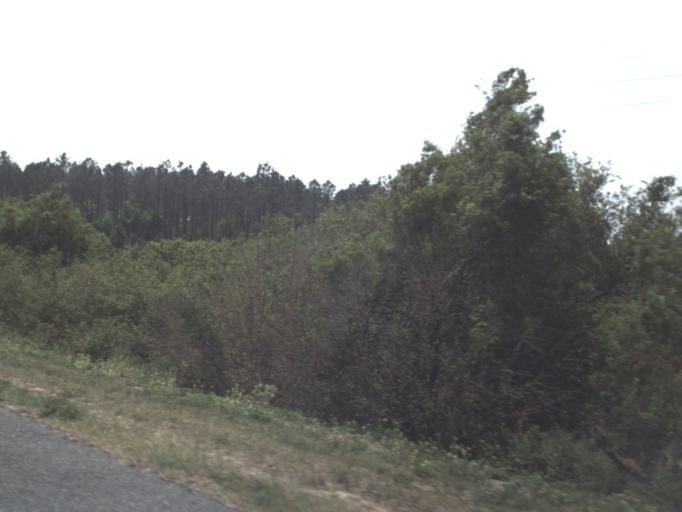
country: US
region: Florida
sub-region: Lake County
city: Howie In The Hills
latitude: 28.6989
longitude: -81.7802
